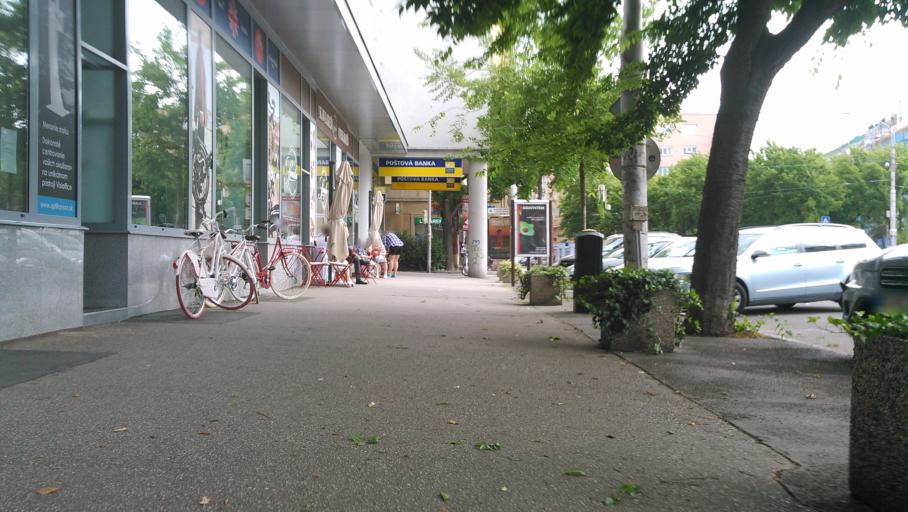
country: SK
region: Bratislavsky
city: Bratislava
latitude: 48.1516
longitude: 17.1193
